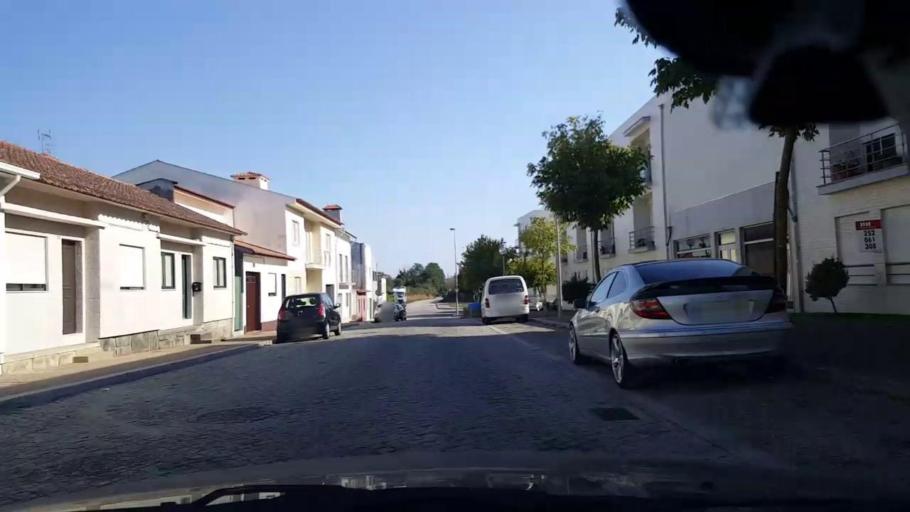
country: PT
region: Porto
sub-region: Vila do Conde
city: Vila do Conde
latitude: 41.3439
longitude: -8.7331
